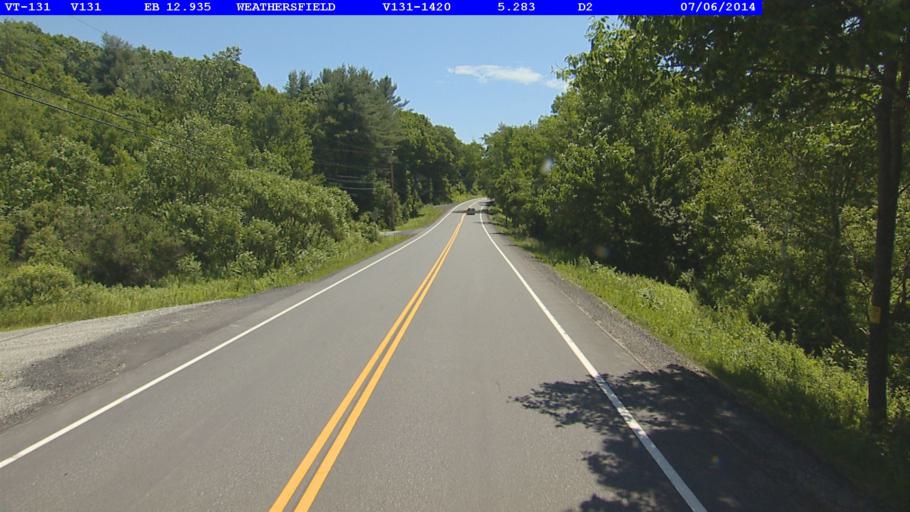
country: US
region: Vermont
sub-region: Windsor County
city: Windsor
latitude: 43.4183
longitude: -72.4648
